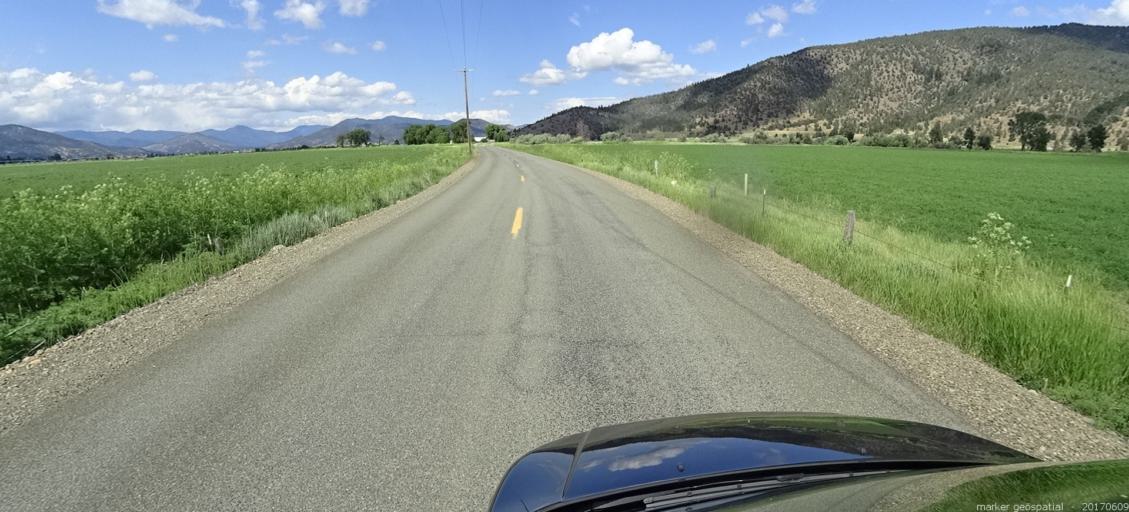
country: US
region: California
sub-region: Siskiyou County
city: Yreka
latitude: 41.5135
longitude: -122.8541
